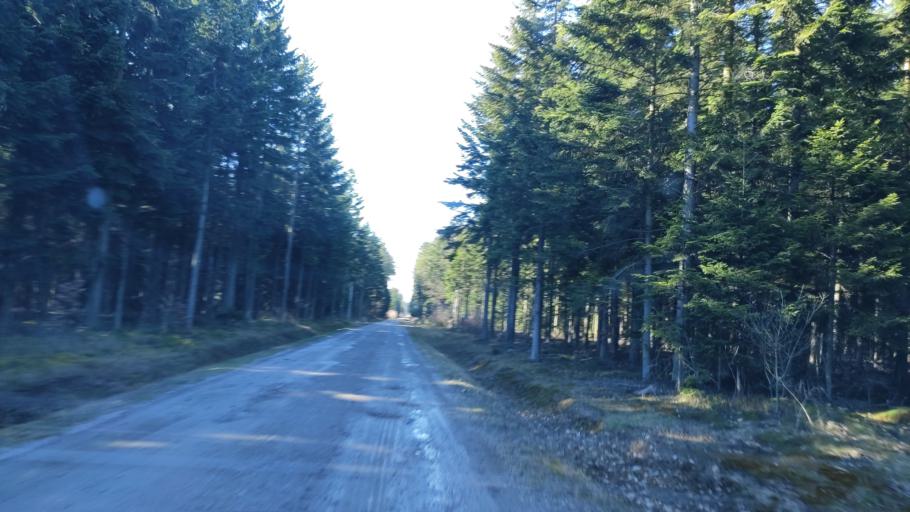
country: PL
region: Masovian Voivodeship
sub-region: Powiat radomski
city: Jedlnia-Letnisko
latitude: 51.4659
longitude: 21.3155
